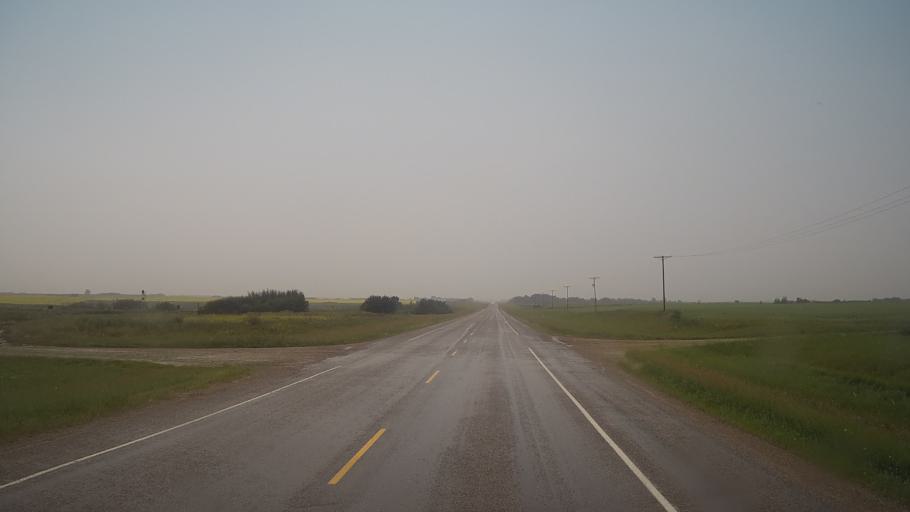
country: CA
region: Saskatchewan
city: Biggar
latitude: 52.1298
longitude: -108.1449
